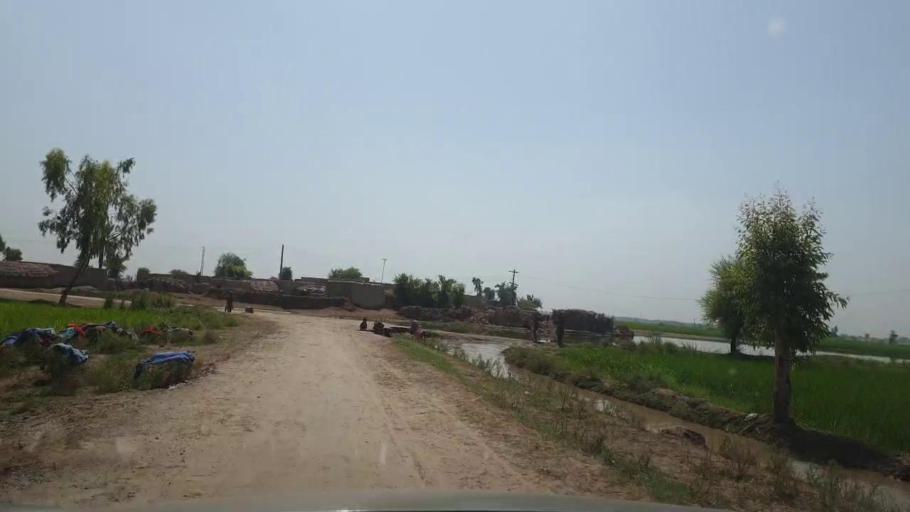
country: PK
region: Sindh
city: Warah
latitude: 27.4844
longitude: 67.7794
